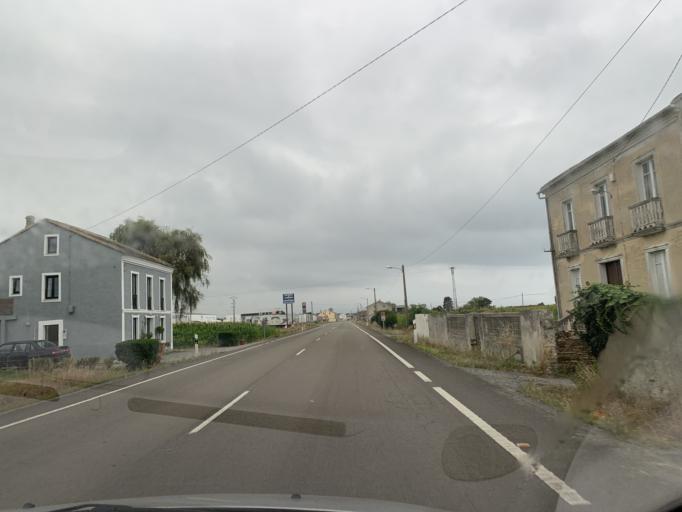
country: ES
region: Galicia
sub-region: Provincia de Lugo
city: Ribadeo
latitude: 43.5491
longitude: -7.1345
